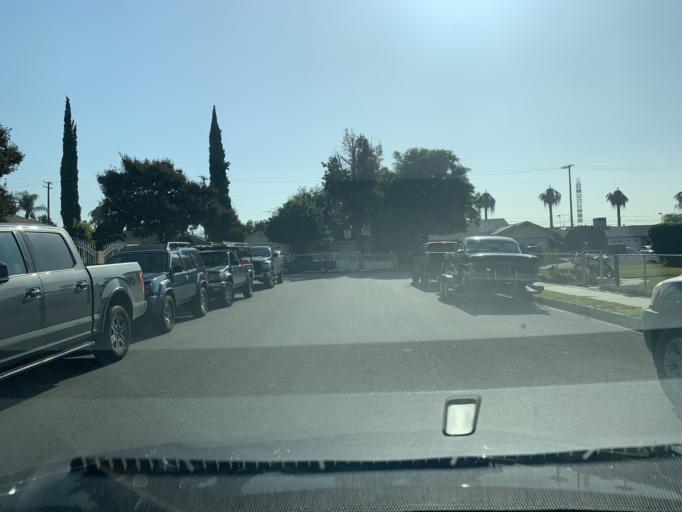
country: US
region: California
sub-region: Los Angeles County
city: Covina
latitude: 34.0764
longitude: -117.8848
